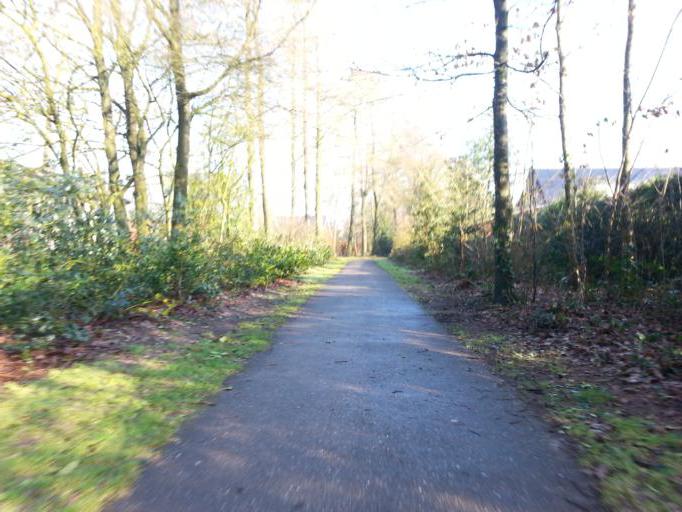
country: NL
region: Utrecht
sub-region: Gemeente Amersfoort
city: Randenbroek
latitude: 52.1175
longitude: 5.4037
